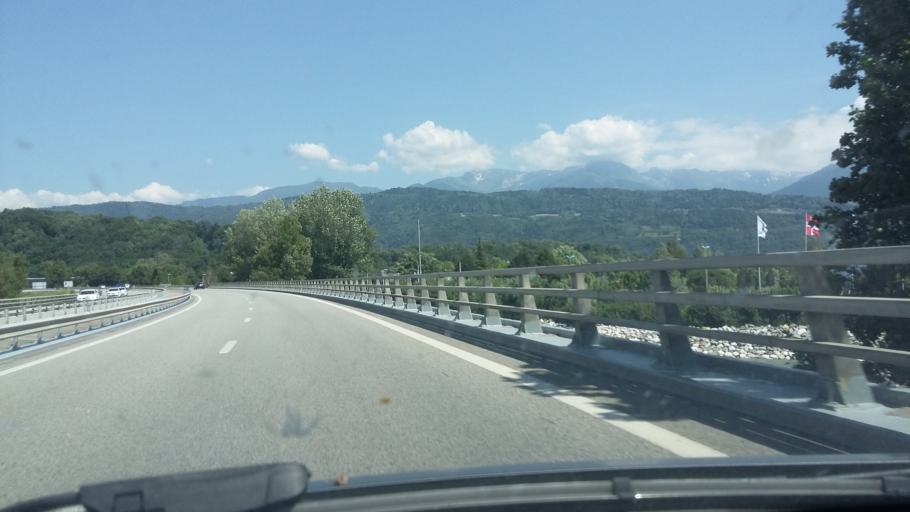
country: FR
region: Rhone-Alpes
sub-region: Departement de la Savoie
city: Montmelian
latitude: 45.4819
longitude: 6.0309
